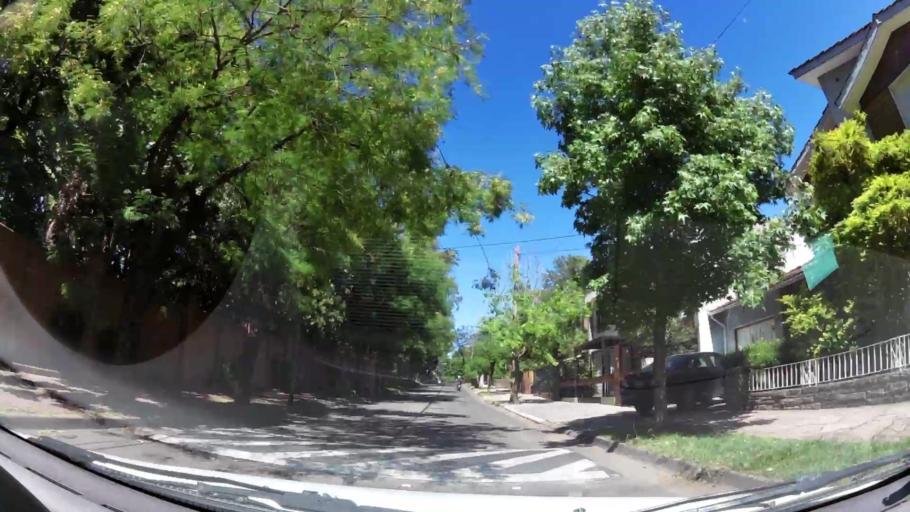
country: AR
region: Buenos Aires
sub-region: Partido de Vicente Lopez
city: Olivos
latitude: -34.5119
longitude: -58.4799
